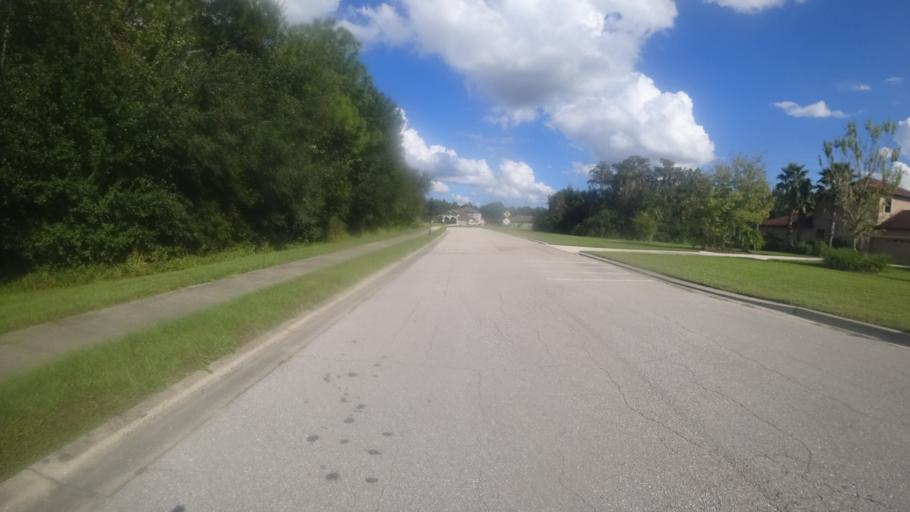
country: US
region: Florida
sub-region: Manatee County
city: Ellenton
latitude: 27.5352
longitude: -82.3860
